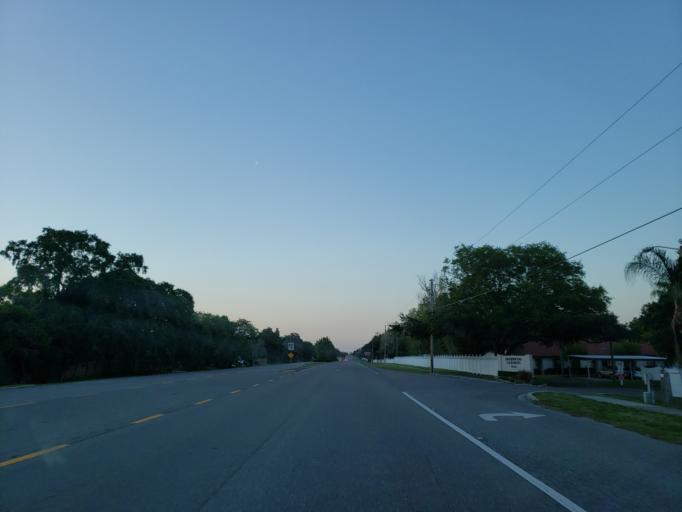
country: US
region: Florida
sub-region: Pinellas County
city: Ridgecrest
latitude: 27.8762
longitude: -82.7952
